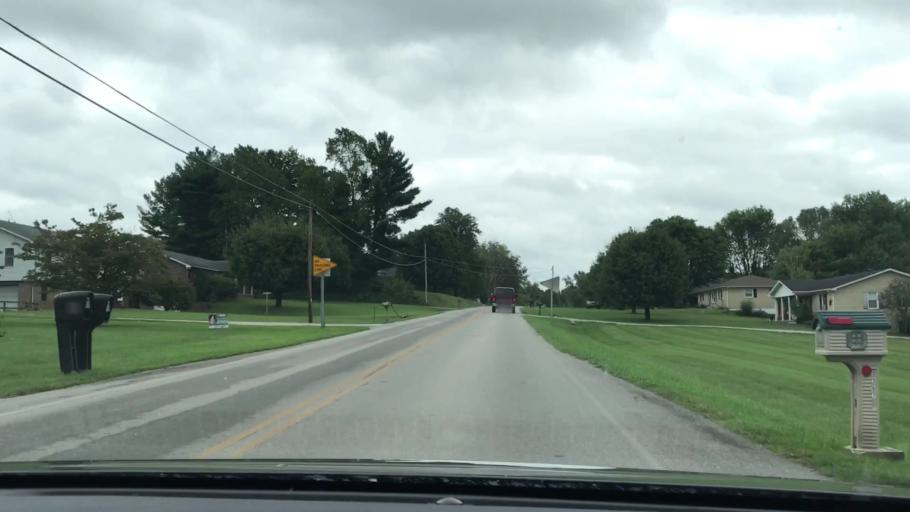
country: US
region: Kentucky
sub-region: Barren County
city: Glasgow
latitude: 36.9643
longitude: -85.8721
